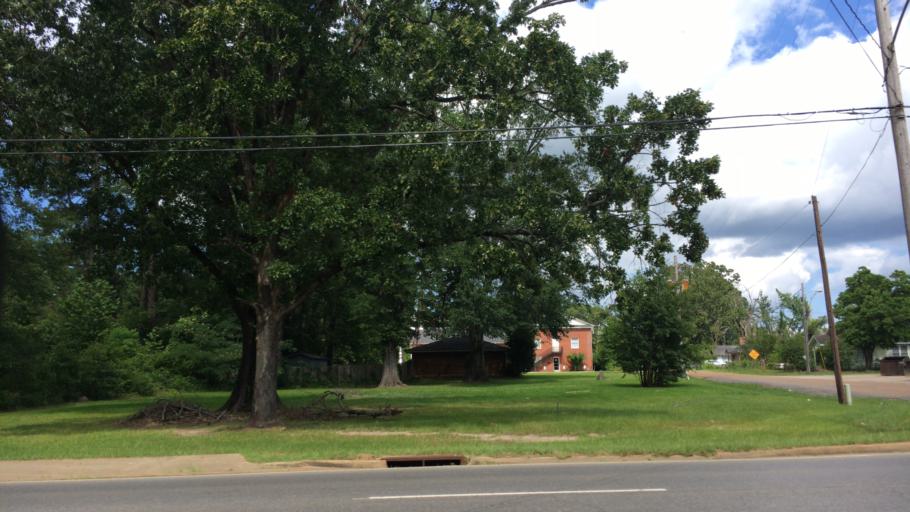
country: US
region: Louisiana
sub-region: Lincoln Parish
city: Ruston
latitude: 32.5114
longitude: -92.6379
